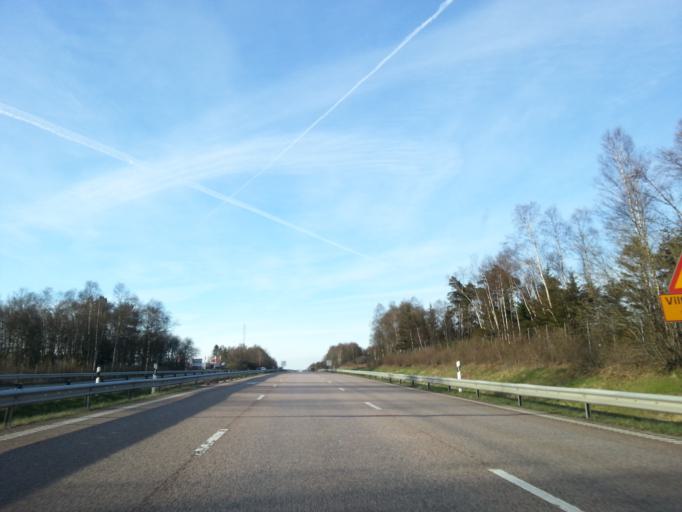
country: SE
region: Skane
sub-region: Bastads Kommun
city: Bastad
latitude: 56.3862
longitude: 12.9374
